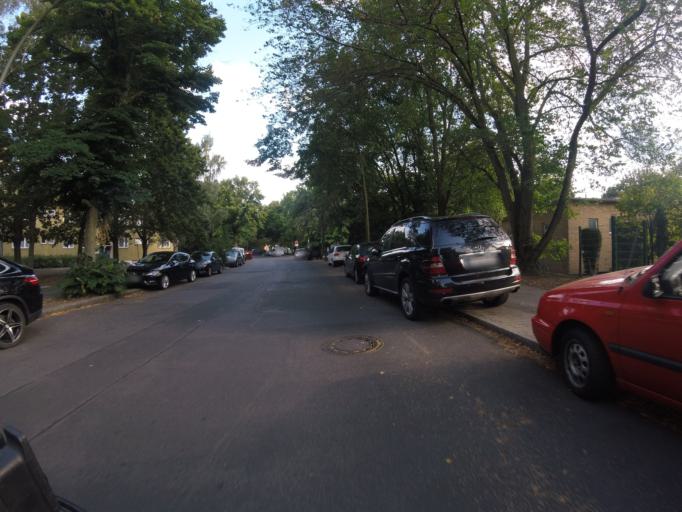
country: DE
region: Berlin
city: Charlottenburg-Nord
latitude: 52.5365
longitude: 13.2795
